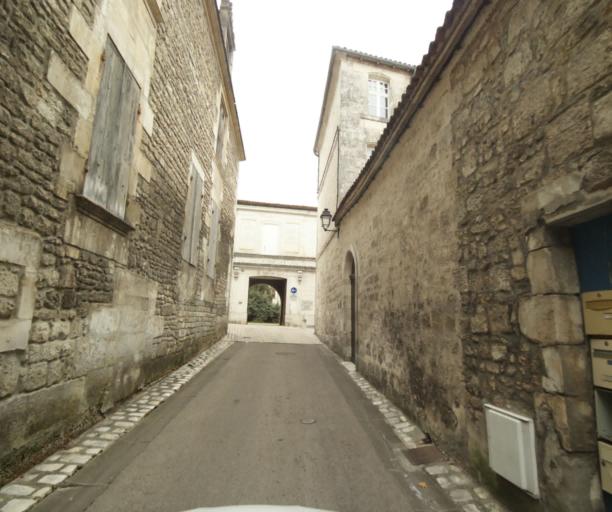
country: FR
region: Poitou-Charentes
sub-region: Departement de la Charente-Maritime
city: Saintes
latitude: 45.7454
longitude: -0.6344
